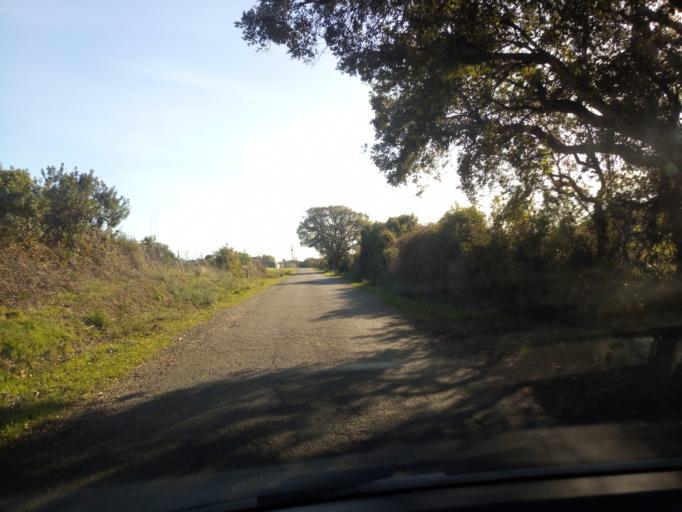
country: FR
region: Corsica
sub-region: Departement de la Haute-Corse
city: Linguizzetta
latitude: 42.2642
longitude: 9.5442
